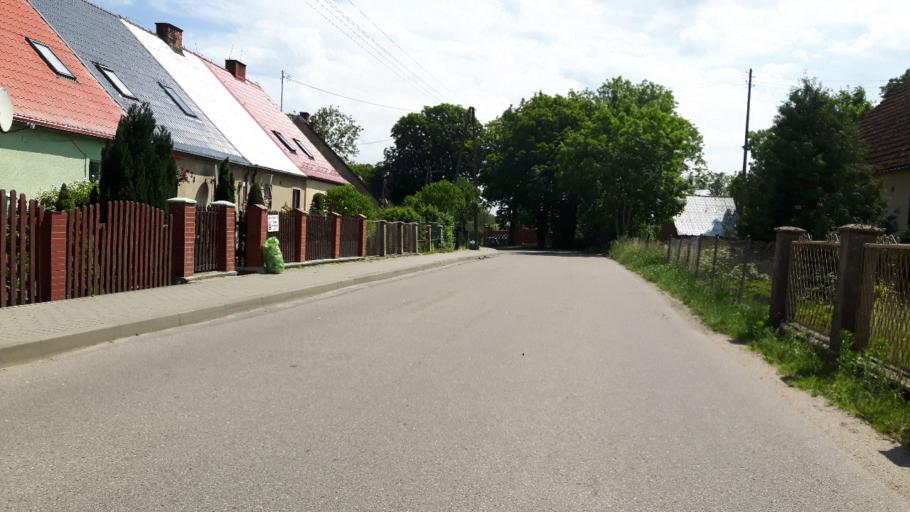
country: PL
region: Pomeranian Voivodeship
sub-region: Powiat wejherowski
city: Choczewo
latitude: 54.7465
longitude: 17.7989
